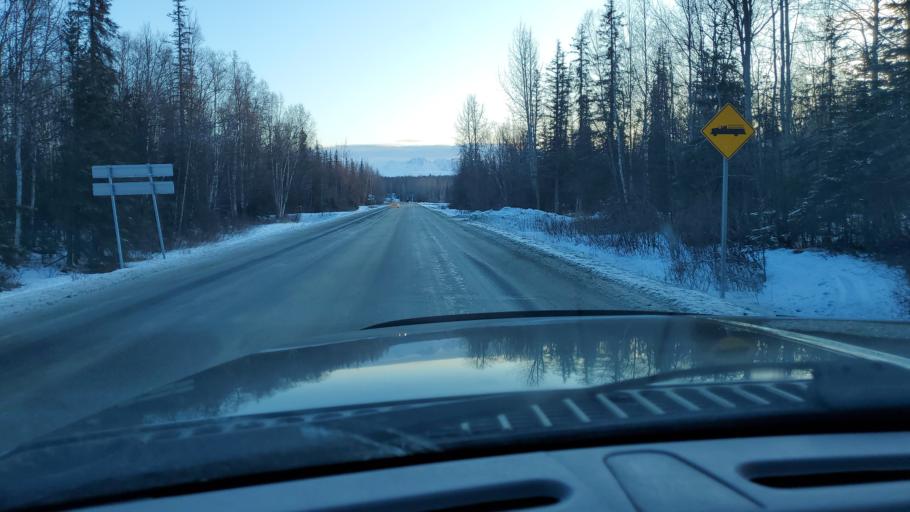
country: US
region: Alaska
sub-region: Matanuska-Susitna Borough
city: Fishhook
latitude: 61.6883
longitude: -149.2413
